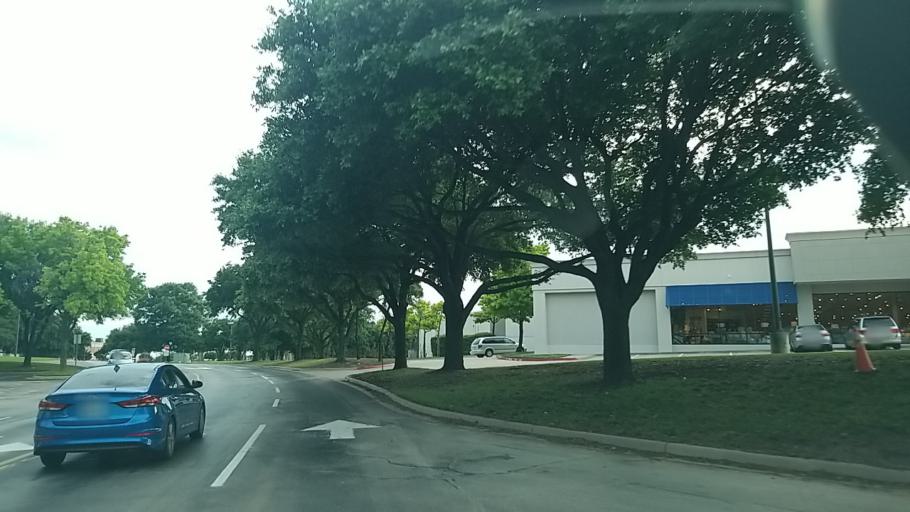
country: US
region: Texas
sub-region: Denton County
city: Lewisville
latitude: 33.0037
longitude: -96.9753
